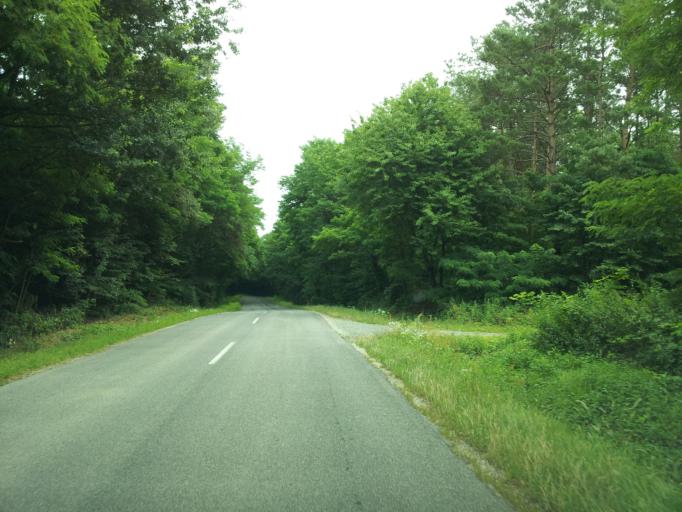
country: HU
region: Vas
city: Vasvar
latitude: 47.0466
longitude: 16.8434
